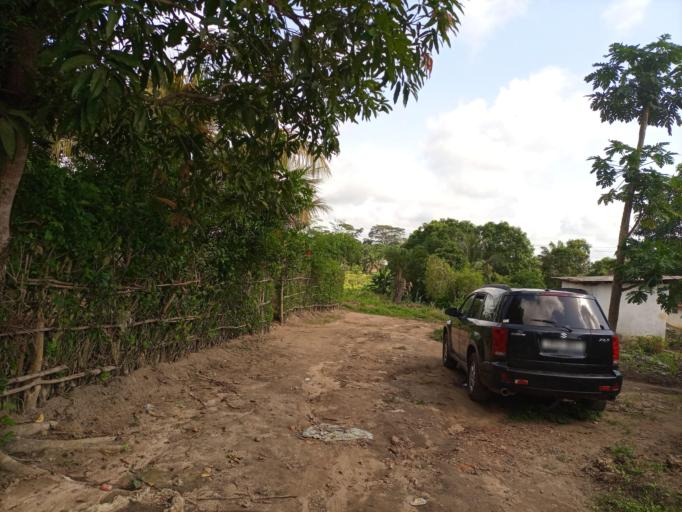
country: SL
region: Southern Province
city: Bo
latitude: 7.9668
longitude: -11.7667
